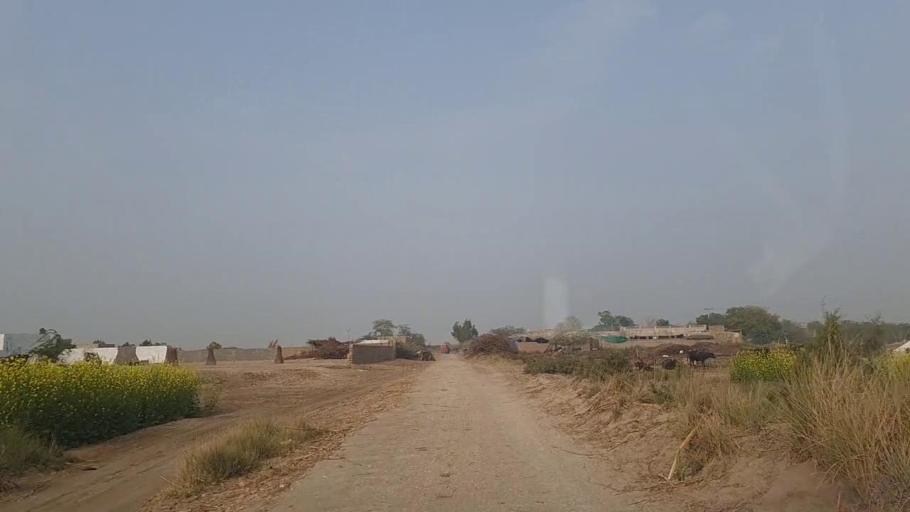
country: PK
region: Sindh
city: Sanghar
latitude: 26.1172
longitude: 68.8963
